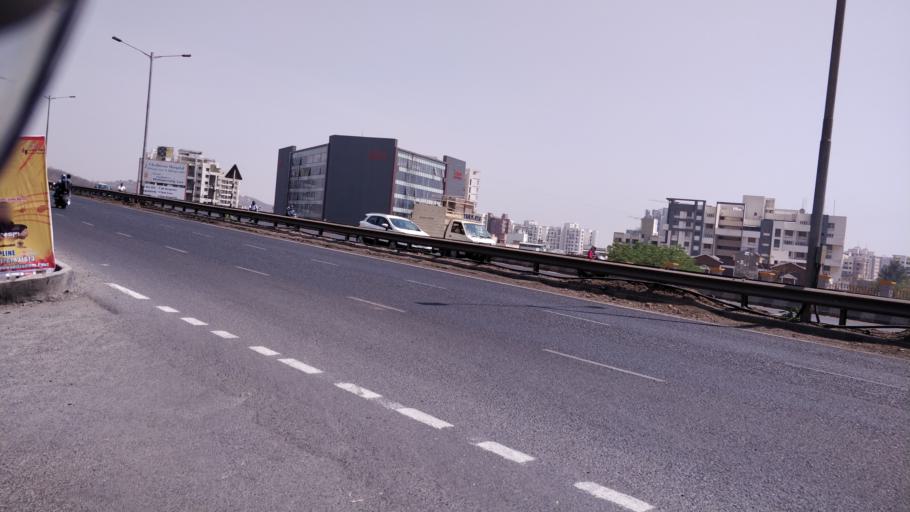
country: IN
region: Maharashtra
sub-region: Pune Division
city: Kharakvasla
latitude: 18.5180
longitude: 73.7687
